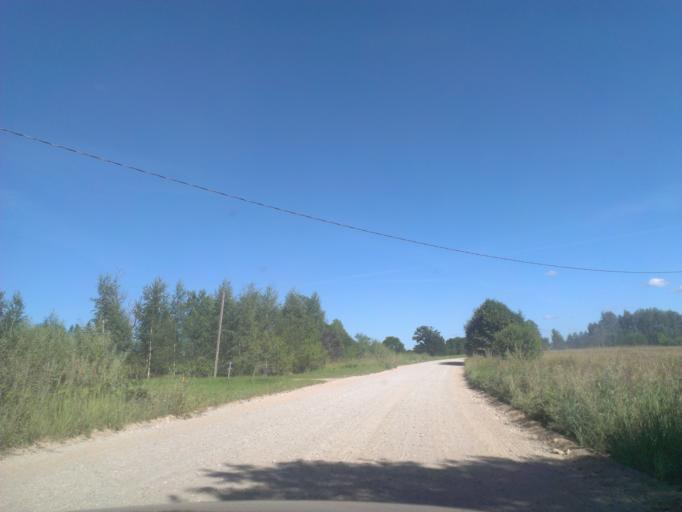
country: LV
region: Malpils
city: Malpils
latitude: 57.0602
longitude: 25.1460
